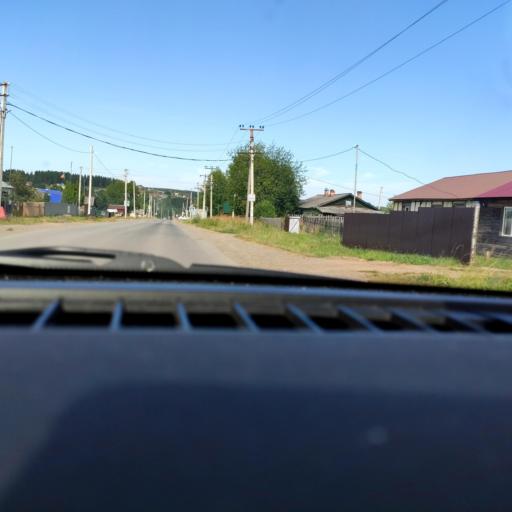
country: RU
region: Perm
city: Polazna
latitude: 58.3423
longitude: 56.2387
